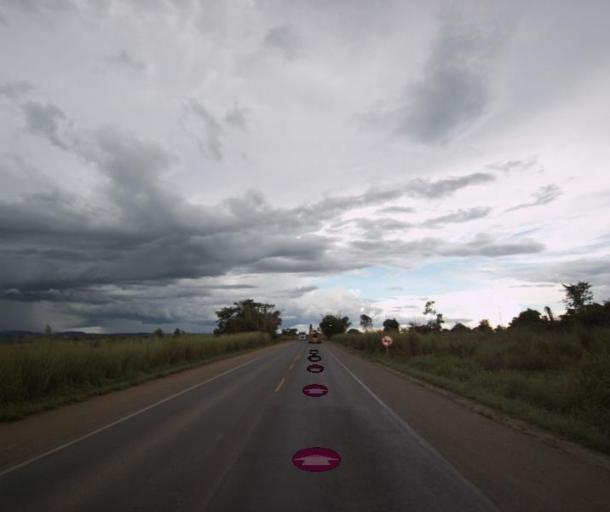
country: BR
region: Goias
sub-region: Itapaci
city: Itapaci
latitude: -15.0134
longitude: -49.4199
